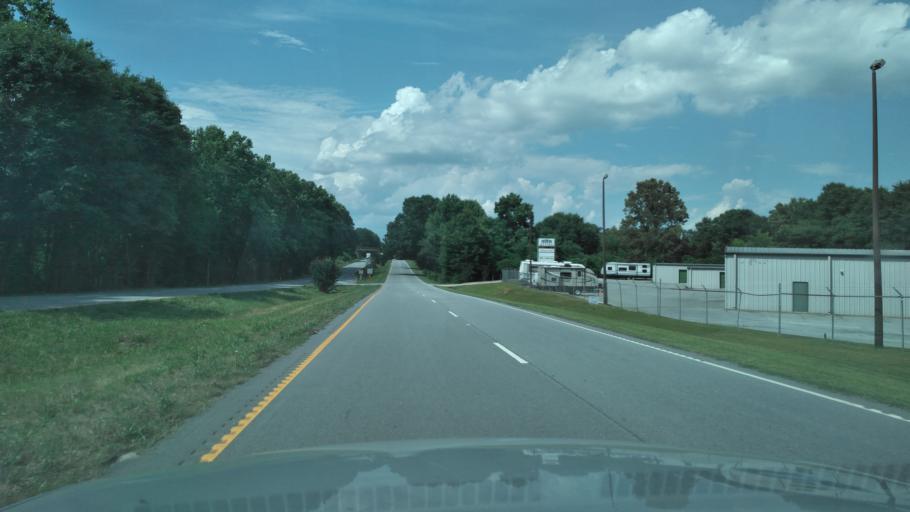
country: US
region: South Carolina
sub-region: Spartanburg County
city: Roebuck
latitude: 34.8633
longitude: -81.9615
